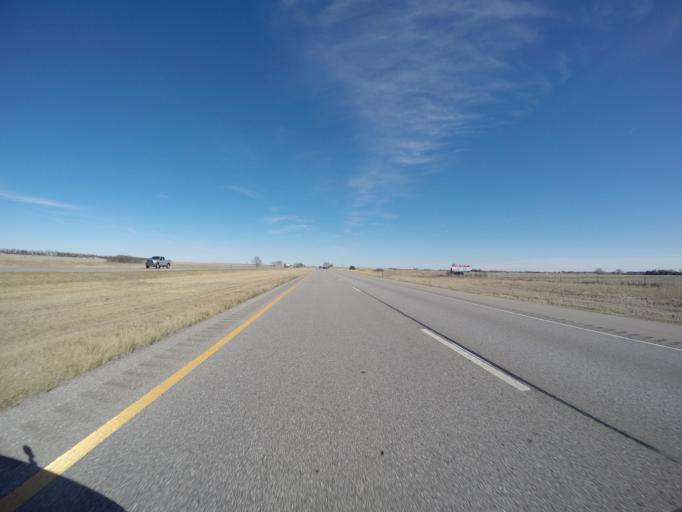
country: US
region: Nebraska
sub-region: Seward County
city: Seward
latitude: 40.8222
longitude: -97.1552
